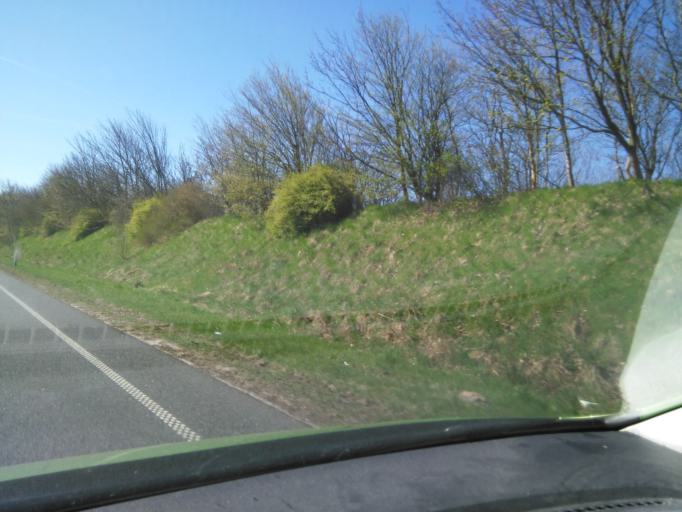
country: DK
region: South Denmark
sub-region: Varde Kommune
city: Varde
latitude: 55.6754
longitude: 8.5756
